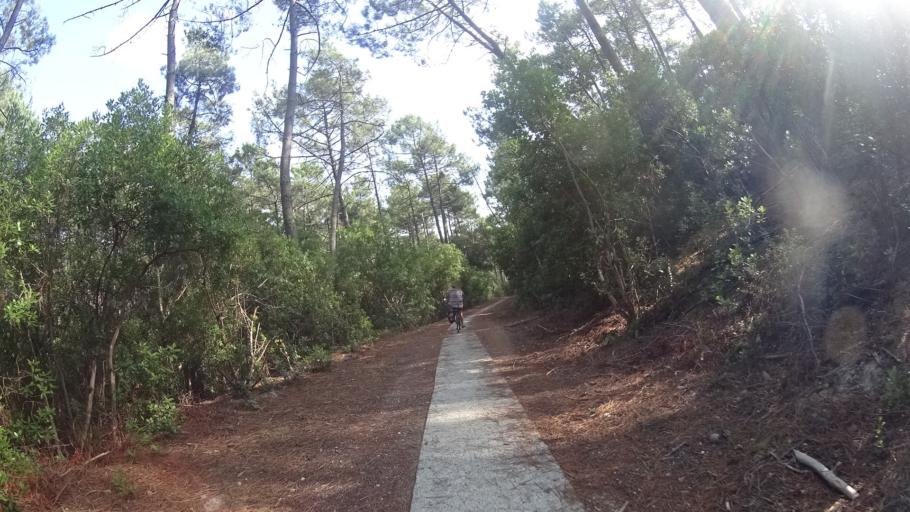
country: FR
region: Aquitaine
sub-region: Departement de la Gironde
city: Lacanau
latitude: 44.9642
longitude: -1.1734
